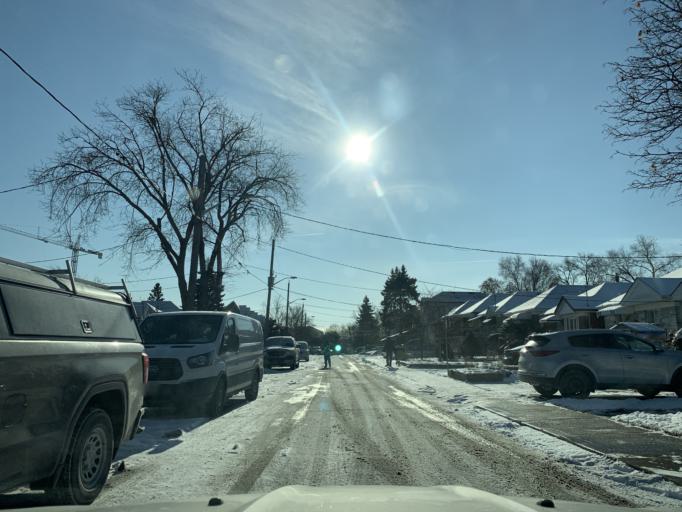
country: CA
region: Ontario
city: Toronto
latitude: 43.6727
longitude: -79.4813
